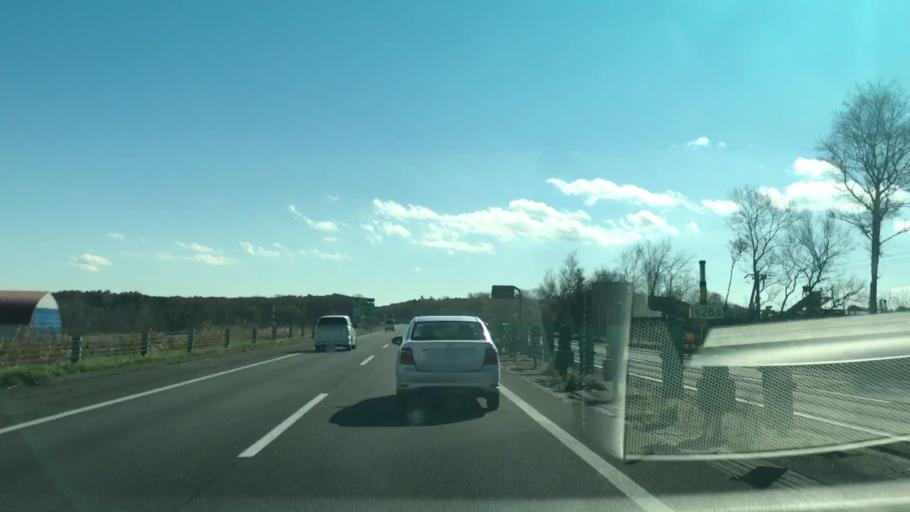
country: JP
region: Hokkaido
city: Chitose
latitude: 42.8670
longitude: 141.5565
